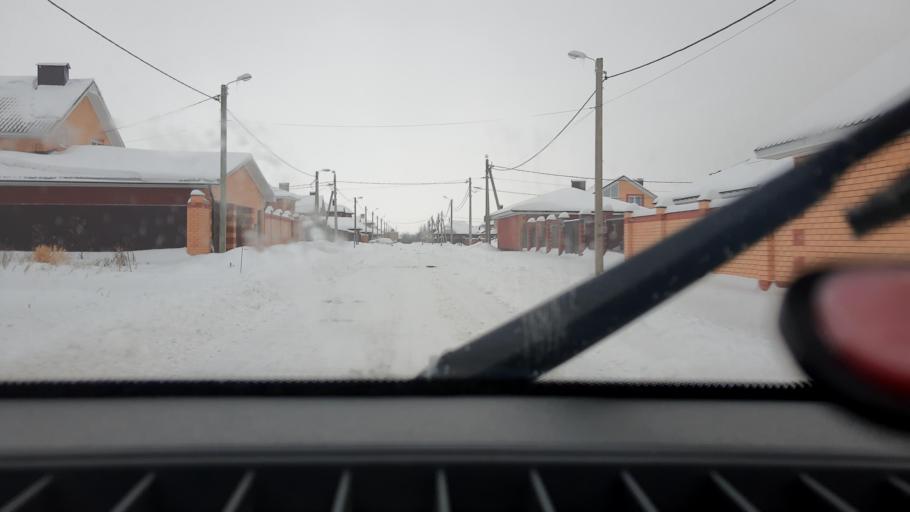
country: RU
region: Bashkortostan
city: Ufa
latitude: 54.6182
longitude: 55.8856
